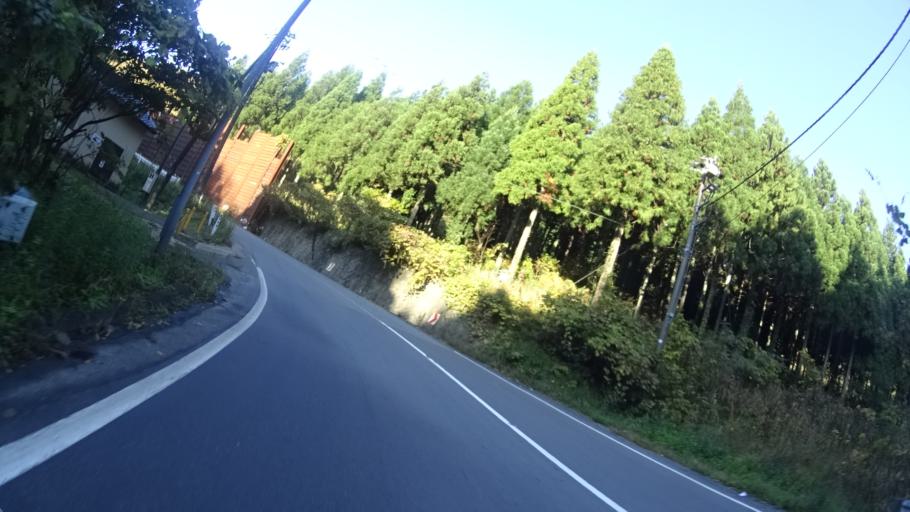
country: JP
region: Fukui
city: Maruoka
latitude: 36.1192
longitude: 136.3218
